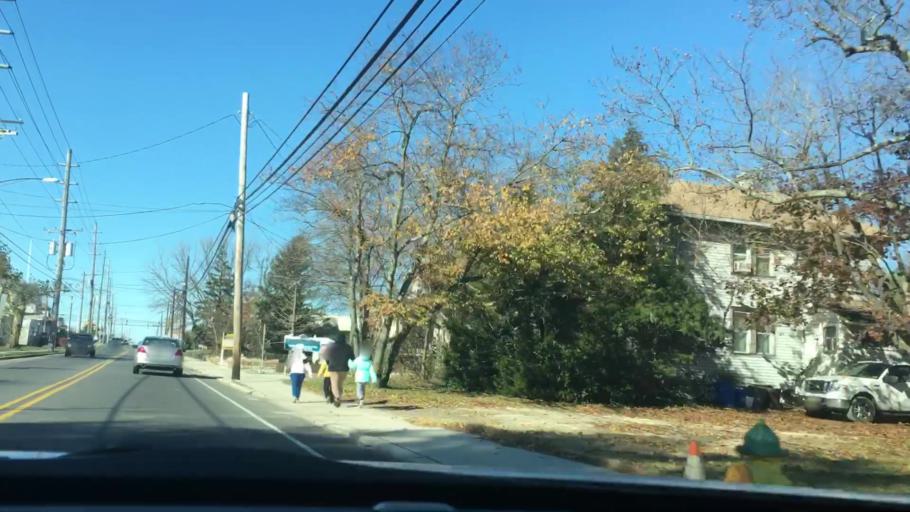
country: US
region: New Jersey
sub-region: Atlantic County
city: Pleasantville
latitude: 39.4067
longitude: -74.5175
